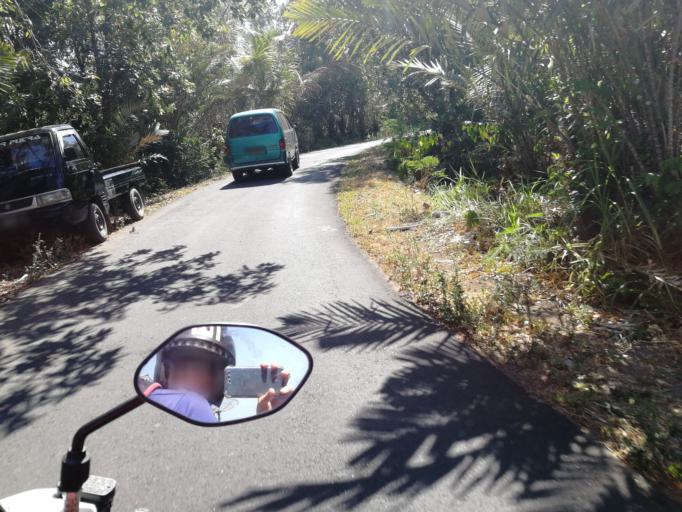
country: ID
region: Bali
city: Banjar Kedisan
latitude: -8.1589
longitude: 115.3058
